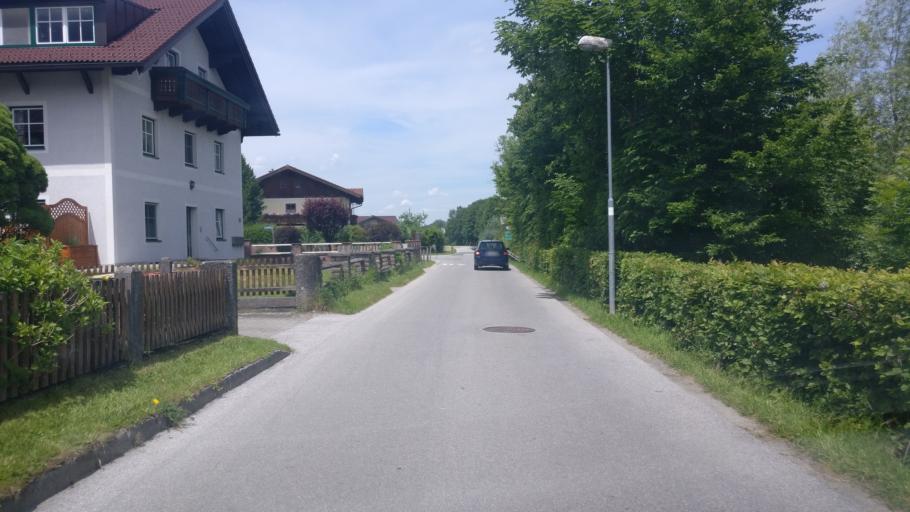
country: AT
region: Salzburg
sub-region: Politischer Bezirk Hallein
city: Kuchl
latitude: 47.6255
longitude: 13.1379
